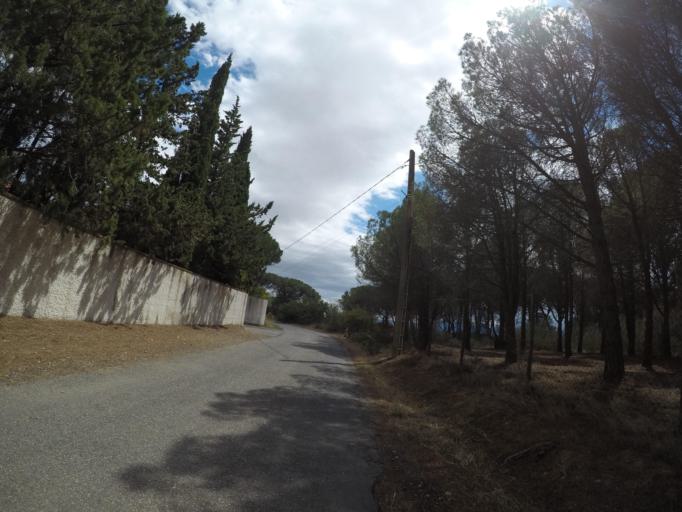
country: FR
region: Languedoc-Roussillon
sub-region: Departement des Pyrenees-Orientales
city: Baho
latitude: 42.7094
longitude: 2.8174
